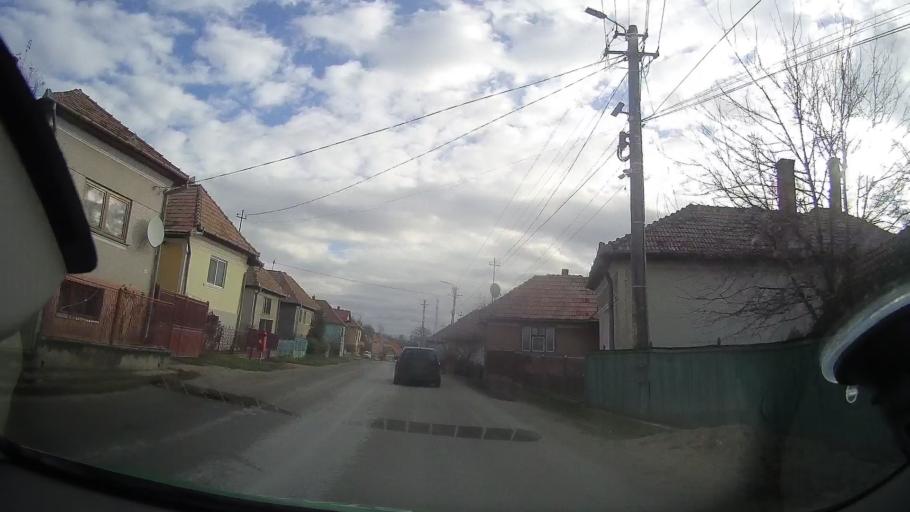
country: RO
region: Cluj
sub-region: Comuna Baisoara
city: Baisoara
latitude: 46.6171
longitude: 23.4572
